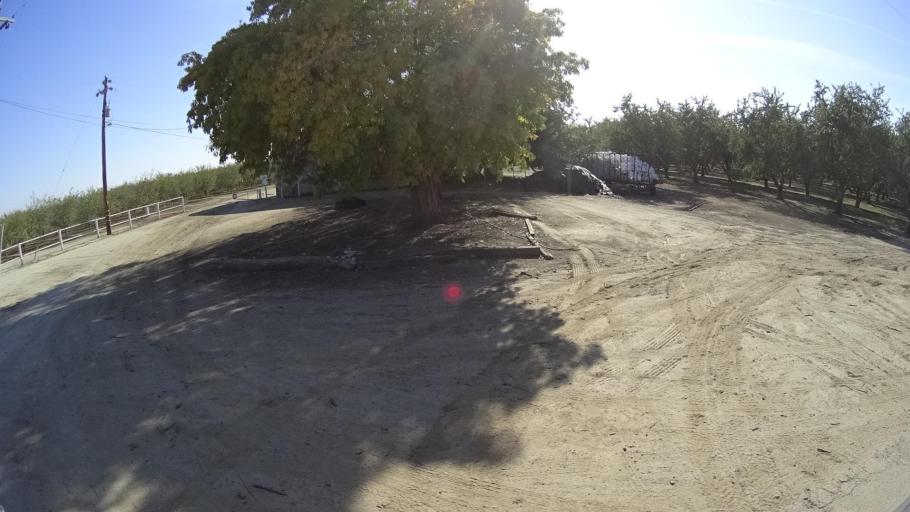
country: US
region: California
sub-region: Kern County
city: Wasco
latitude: 35.6669
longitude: -119.3398
